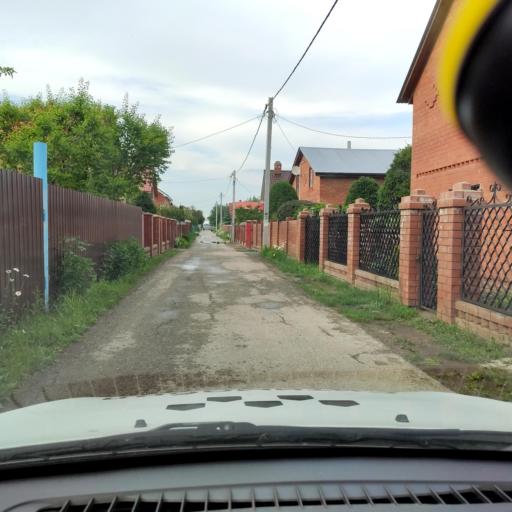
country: RU
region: Samara
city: Podstepki
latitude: 53.5782
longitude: 49.0795
